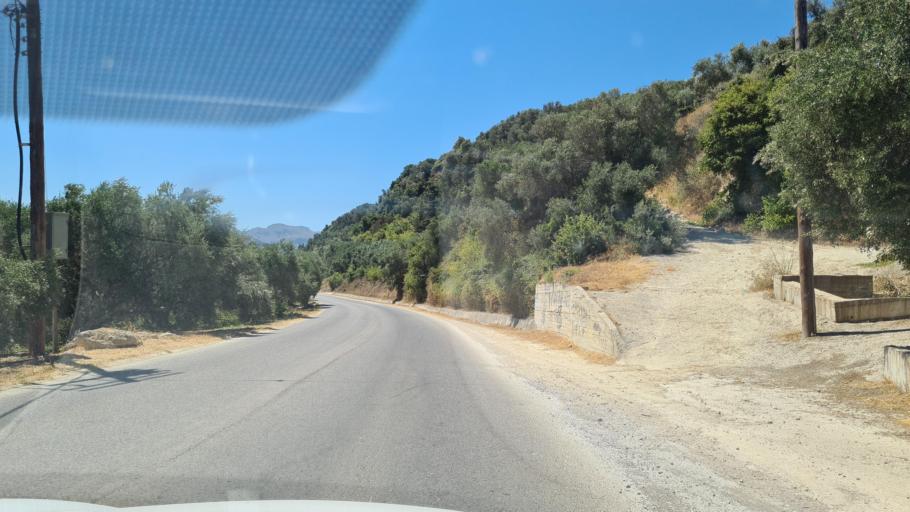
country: GR
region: Crete
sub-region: Nomos Chanias
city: Kissamos
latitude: 35.4771
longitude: 23.6909
